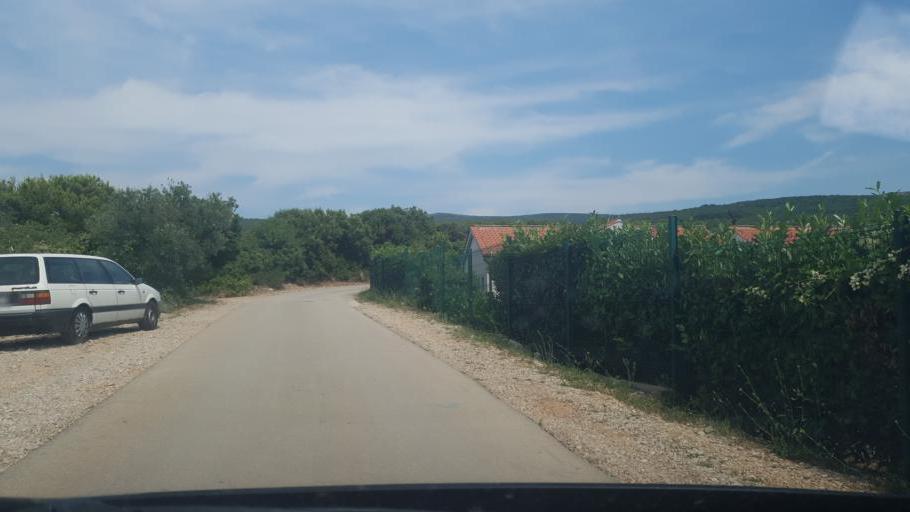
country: HR
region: Primorsko-Goranska
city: Punat
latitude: 45.0088
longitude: 14.6253
